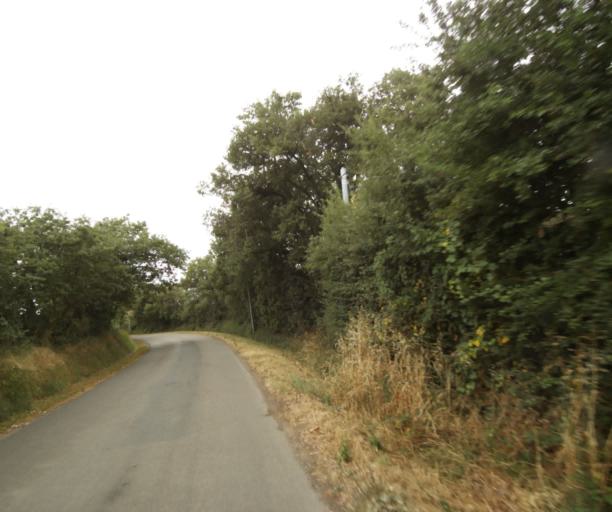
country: FR
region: Pays de la Loire
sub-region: Departement de la Vendee
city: Chateau-d'Olonne
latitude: 46.5024
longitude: -1.7232
